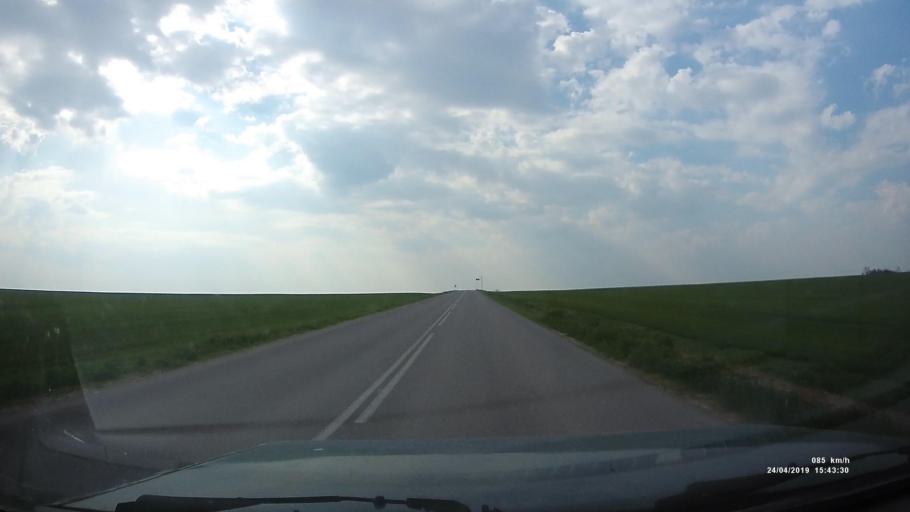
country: RU
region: Kalmykiya
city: Yashalta
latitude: 46.5831
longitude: 42.7715
